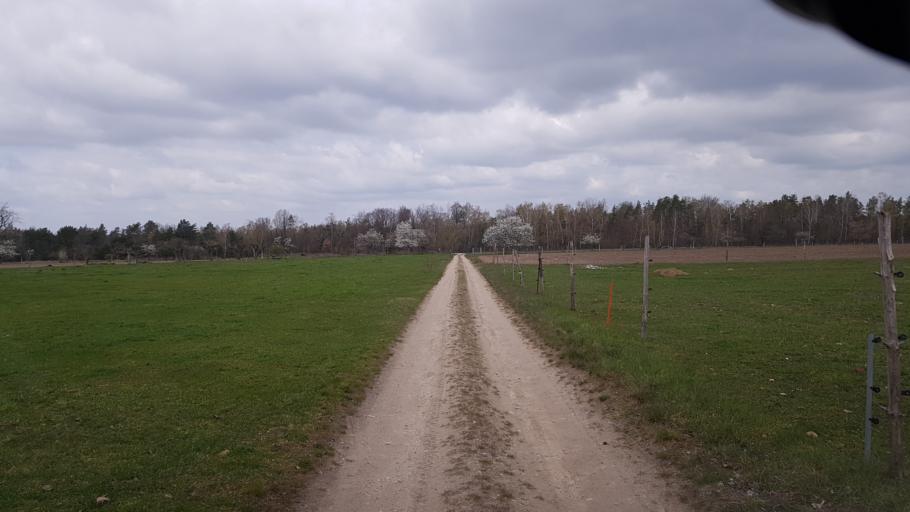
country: DE
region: Brandenburg
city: Hohenleipisch
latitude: 51.5044
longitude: 13.5481
